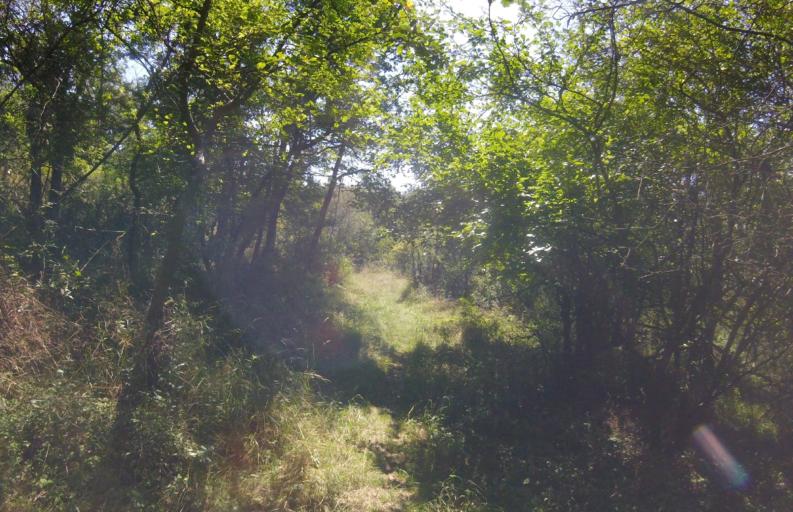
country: HU
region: Pest
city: Szob
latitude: 47.8831
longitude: 18.8710
